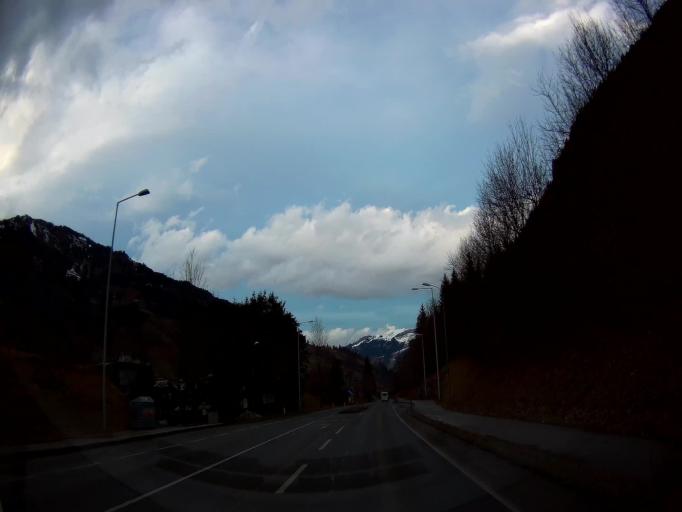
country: AT
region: Salzburg
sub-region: Politischer Bezirk Sankt Johann im Pongau
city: Bad Hofgastein
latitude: 47.1861
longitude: 13.1010
